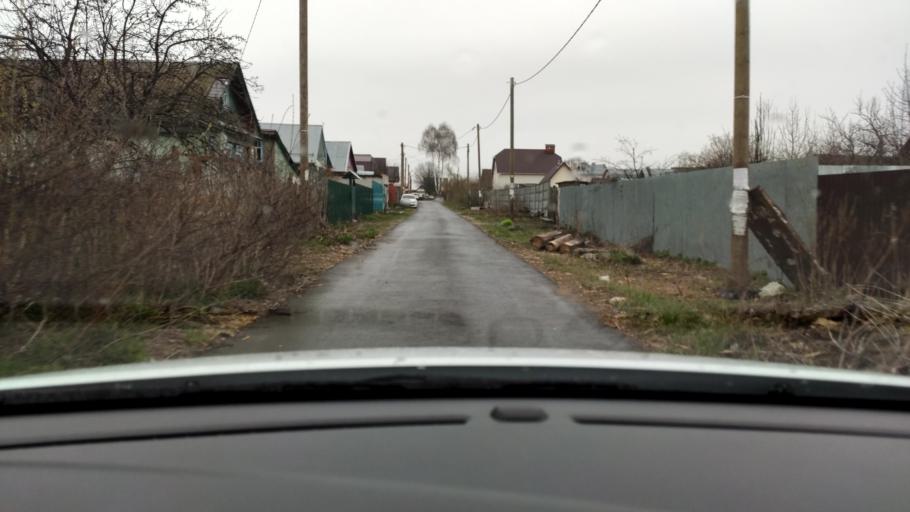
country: RU
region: Tatarstan
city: Osinovo
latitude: 55.8282
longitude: 48.8684
